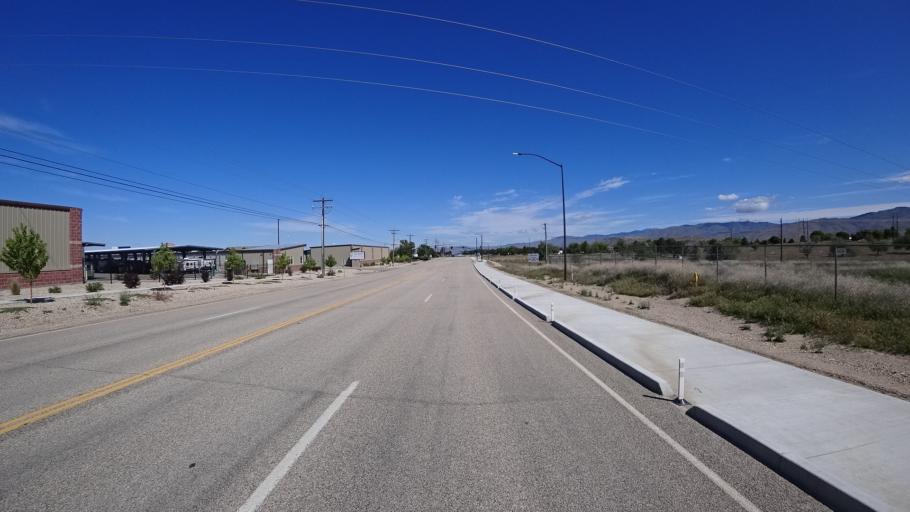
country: US
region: Idaho
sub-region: Ada County
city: Boise
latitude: 43.5375
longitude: -116.1541
